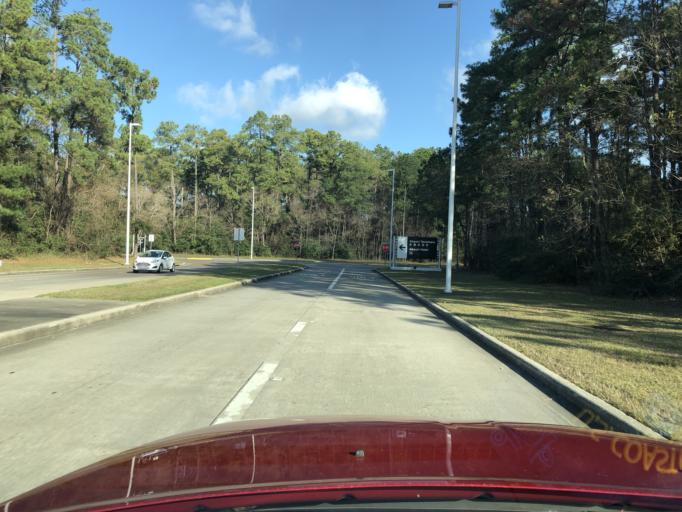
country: US
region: Texas
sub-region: Harris County
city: Aldine
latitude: 29.9718
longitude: -95.3354
